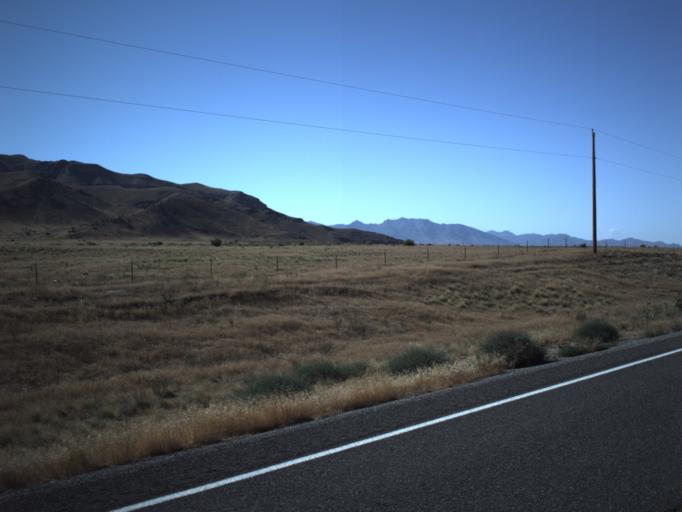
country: US
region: Utah
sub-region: Millard County
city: Delta
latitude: 39.6232
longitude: -112.3134
